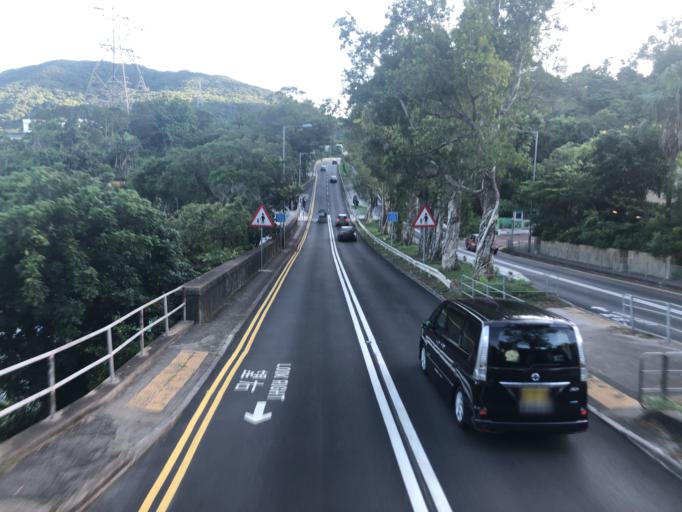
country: HK
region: Sai Kung
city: Sai Kung
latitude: 22.3368
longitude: 114.2427
